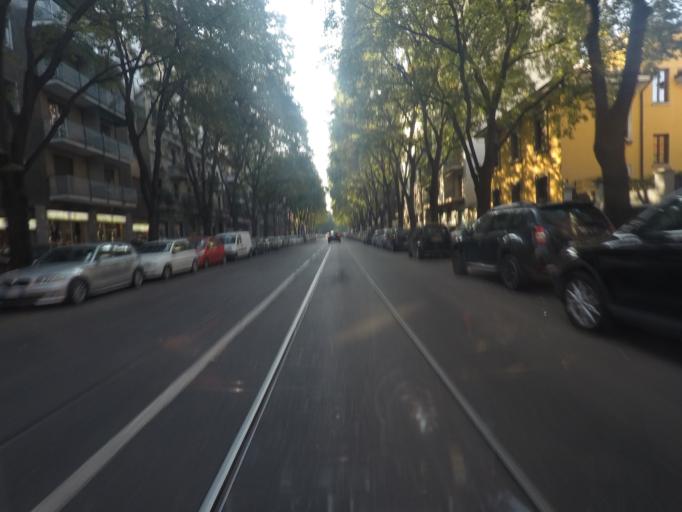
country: IT
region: Lombardy
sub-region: Citta metropolitana di Milano
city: Milano
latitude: 45.4879
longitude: 9.2299
